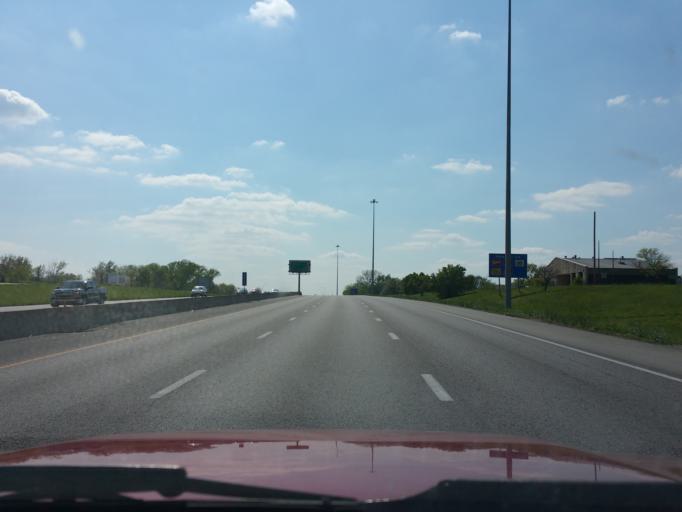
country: US
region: Kansas
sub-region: Johnson County
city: Shawnee
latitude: 39.1062
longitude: -94.7478
